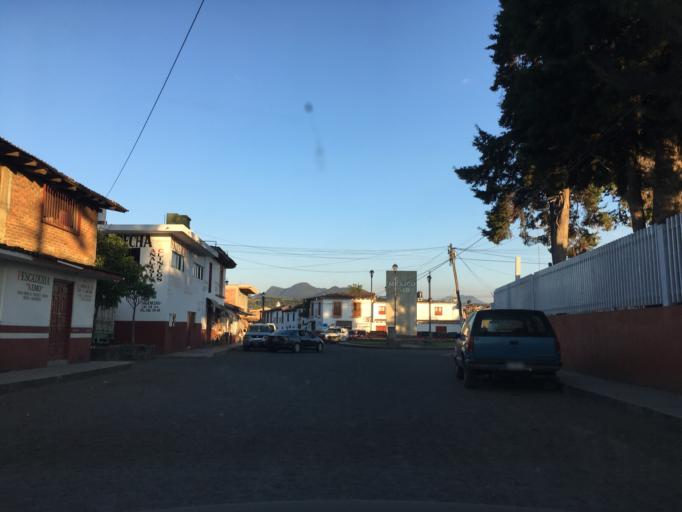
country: MX
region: Michoacan
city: Patzcuaro
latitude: 19.5133
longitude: -101.6172
